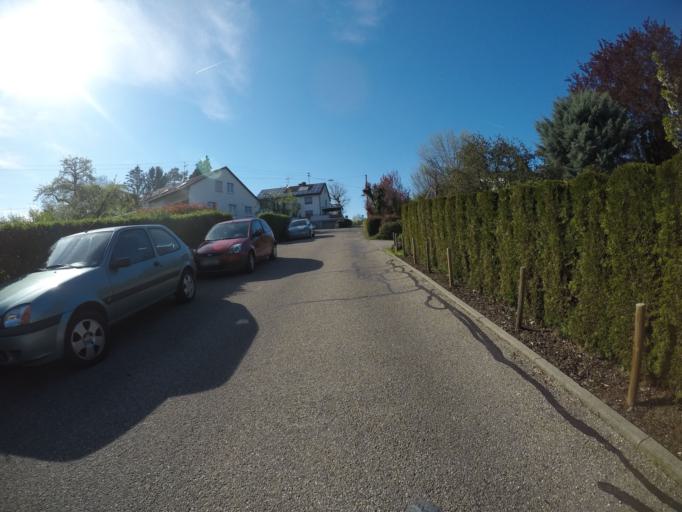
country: DE
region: Baden-Wuerttemberg
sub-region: Regierungsbezirk Stuttgart
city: Neckartailfingen
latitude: 48.6111
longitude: 9.2576
